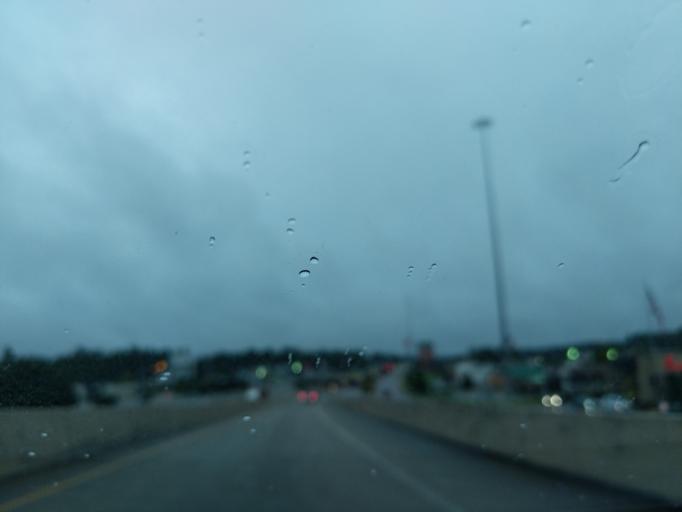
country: US
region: Texas
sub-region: Angelina County
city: Lufkin
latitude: 31.3104
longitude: -94.7255
